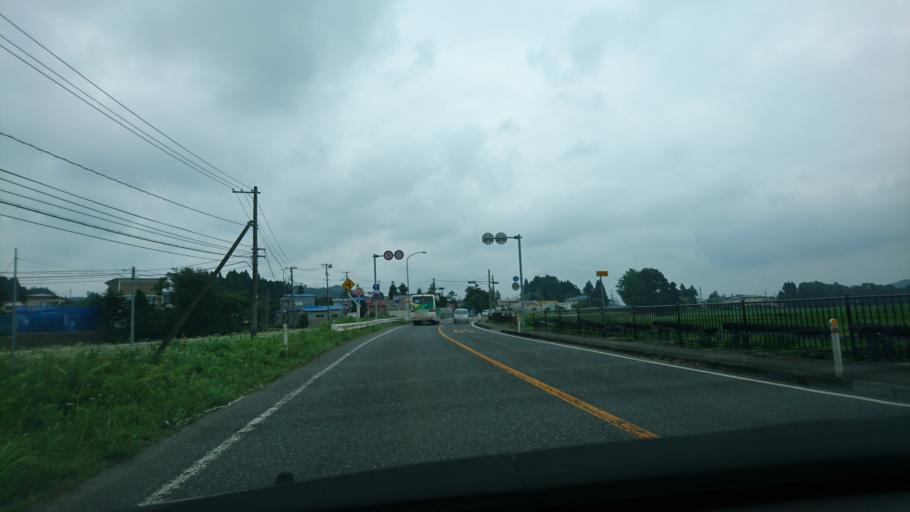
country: JP
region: Miyagi
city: Furukawa
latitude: 38.7135
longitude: 140.8287
